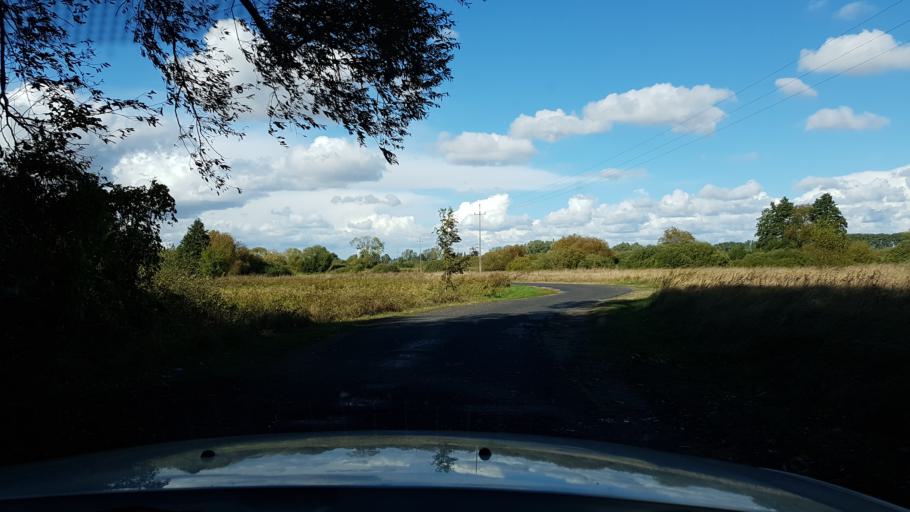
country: PL
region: West Pomeranian Voivodeship
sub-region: Powiat gryfinski
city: Gryfino
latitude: 53.2727
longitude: 14.4975
